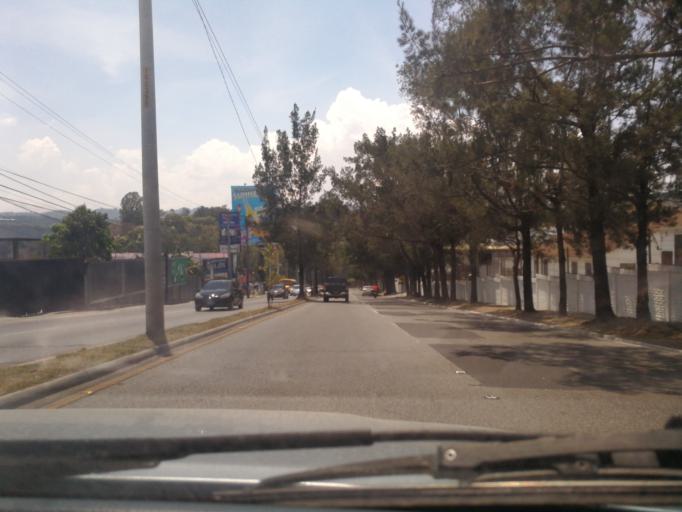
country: GT
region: Guatemala
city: Guatemala City
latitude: 14.6214
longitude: -90.4965
